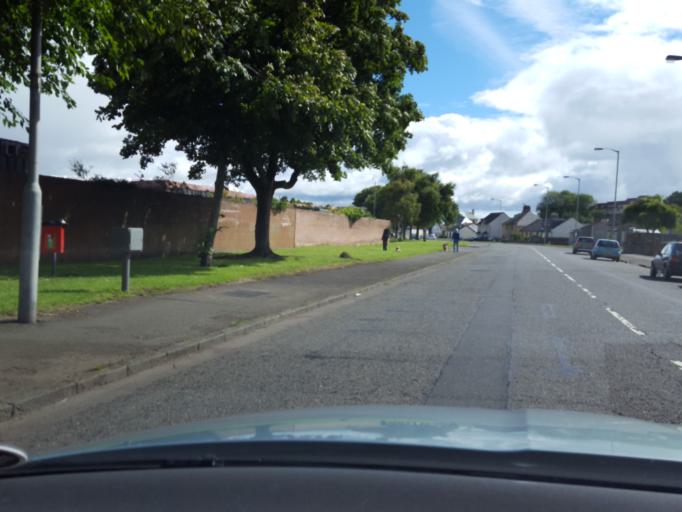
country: GB
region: Scotland
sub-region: Falkirk
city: Bo'ness
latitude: 56.0166
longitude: -3.5886
